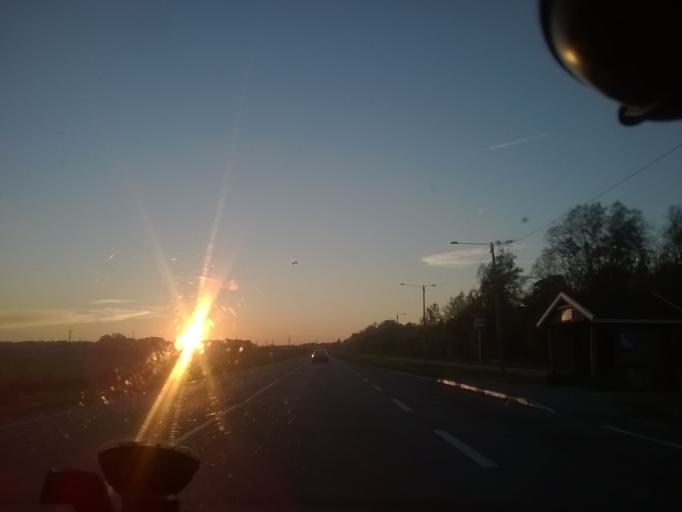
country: EE
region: Laeaene
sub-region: Ridala Parish
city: Uuemoisa
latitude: 58.9560
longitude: 23.7721
